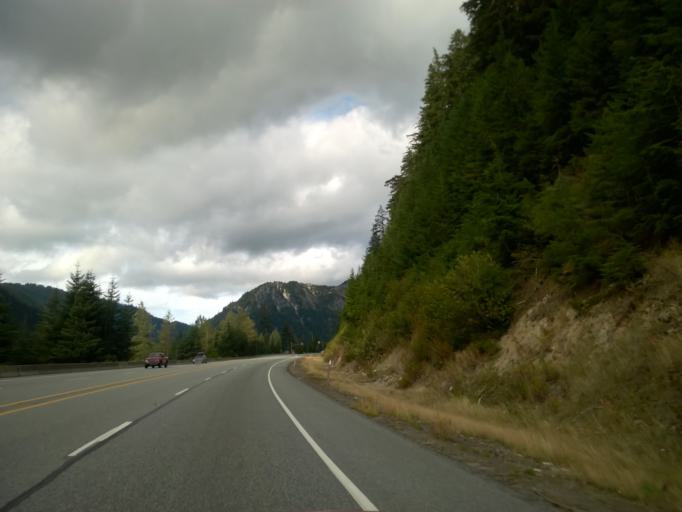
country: US
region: Washington
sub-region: Chelan County
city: Leavenworth
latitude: 47.7291
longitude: -121.1368
